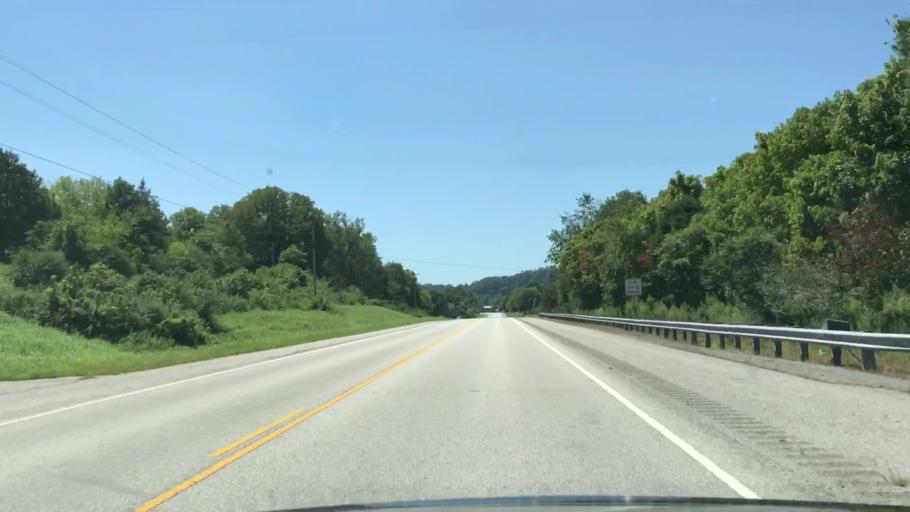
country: US
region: Tennessee
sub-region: Jackson County
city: Gainesboro
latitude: 36.4321
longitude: -85.6333
